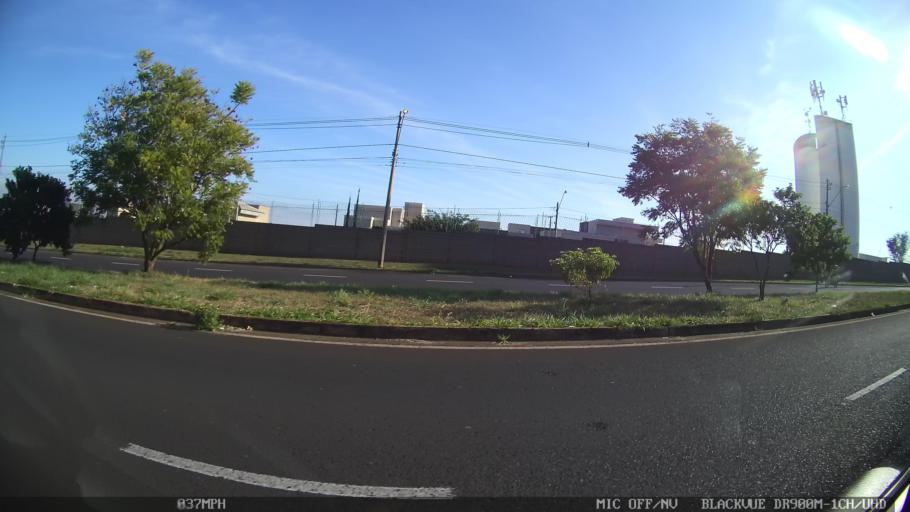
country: BR
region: Sao Paulo
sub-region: Sao Jose Do Rio Preto
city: Sao Jose do Rio Preto
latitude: -20.7765
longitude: -49.3402
